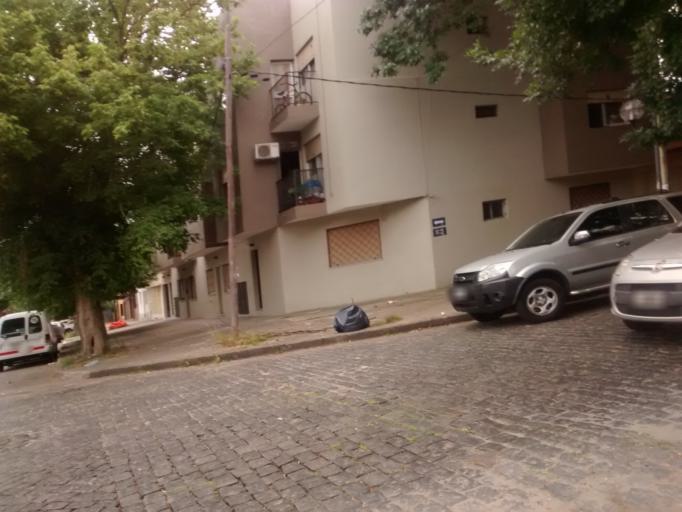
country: AR
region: Buenos Aires
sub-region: Partido de La Plata
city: La Plata
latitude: -34.9302
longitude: -57.9474
